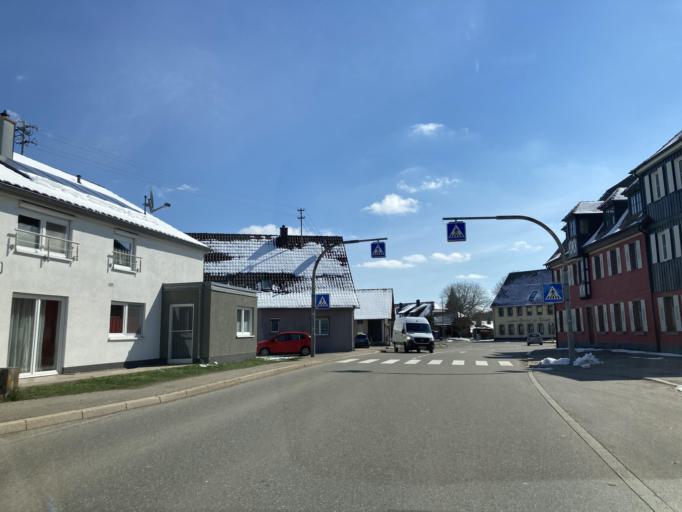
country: DE
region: Baden-Wuerttemberg
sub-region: Freiburg Region
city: Oberndorf
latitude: 48.2814
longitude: 8.5393
